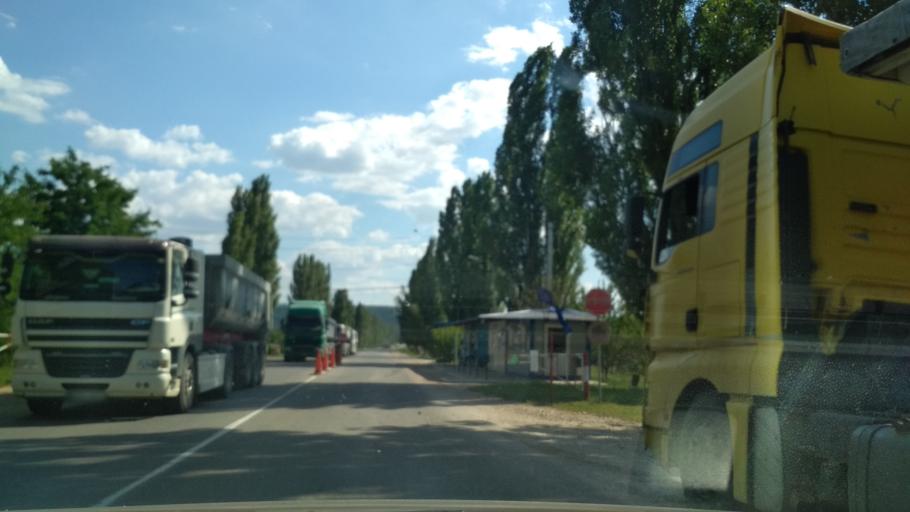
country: MD
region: Chisinau
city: Vadul lui Voda
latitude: 47.1016
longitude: 29.0986
